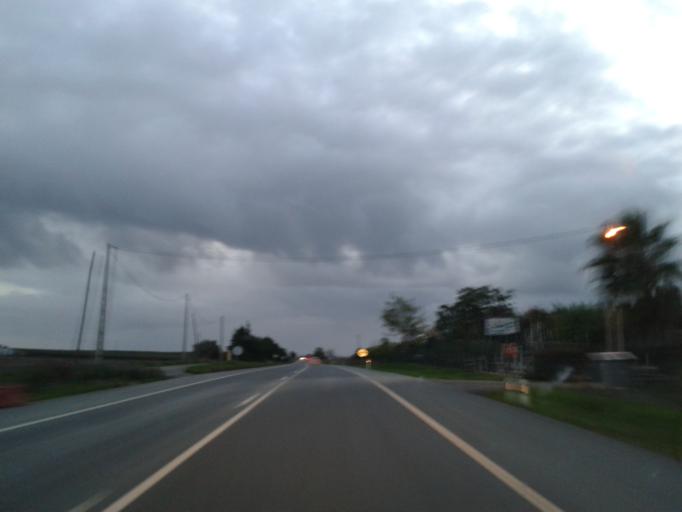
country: PT
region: Beja
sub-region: Beja
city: Beja
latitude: 37.9915
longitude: -7.8684
